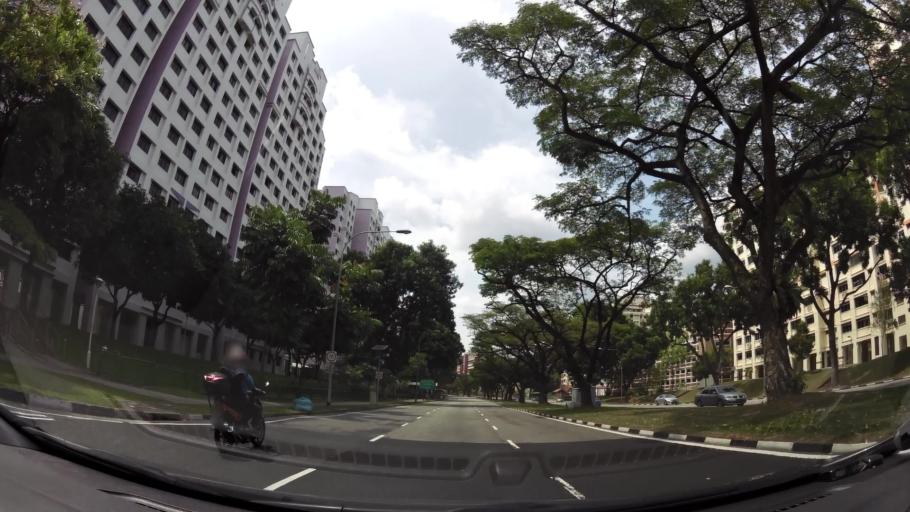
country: MY
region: Johor
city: Johor Bahru
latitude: 1.3456
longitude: 103.7022
